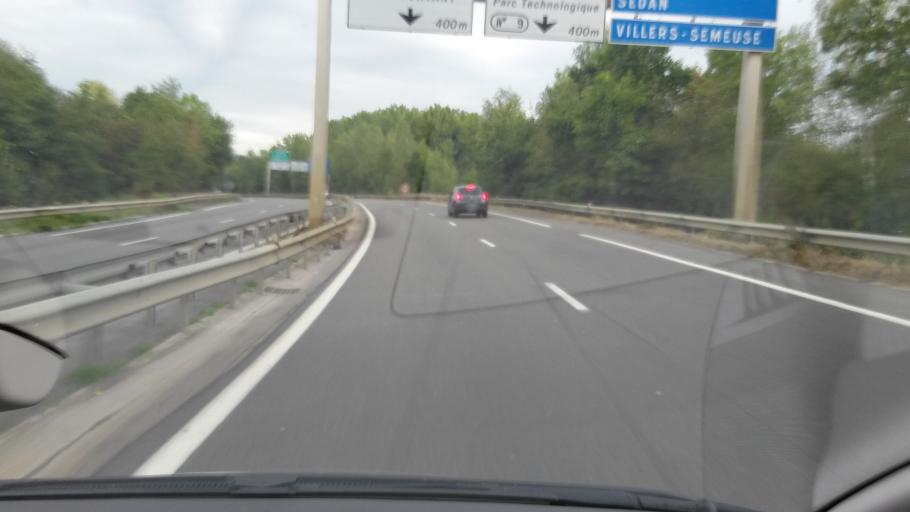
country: FR
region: Champagne-Ardenne
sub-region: Departement des Ardennes
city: La Francheville
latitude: 49.7297
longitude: 4.7190
